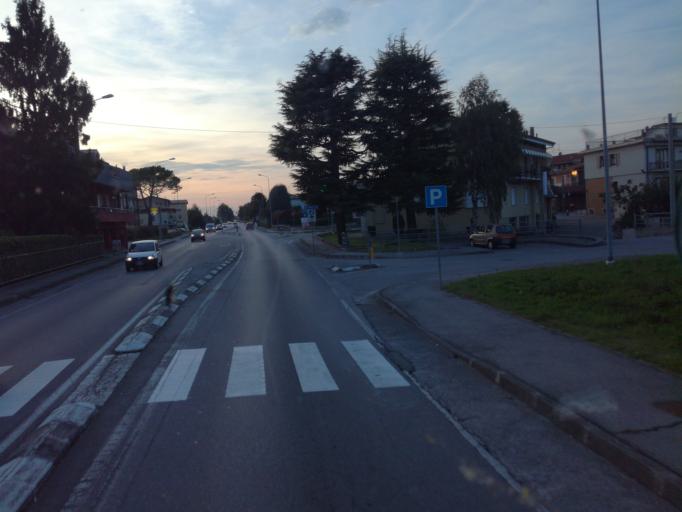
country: IT
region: Lombardy
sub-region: Provincia di Lecco
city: Barzago
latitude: 45.7533
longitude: 9.3166
